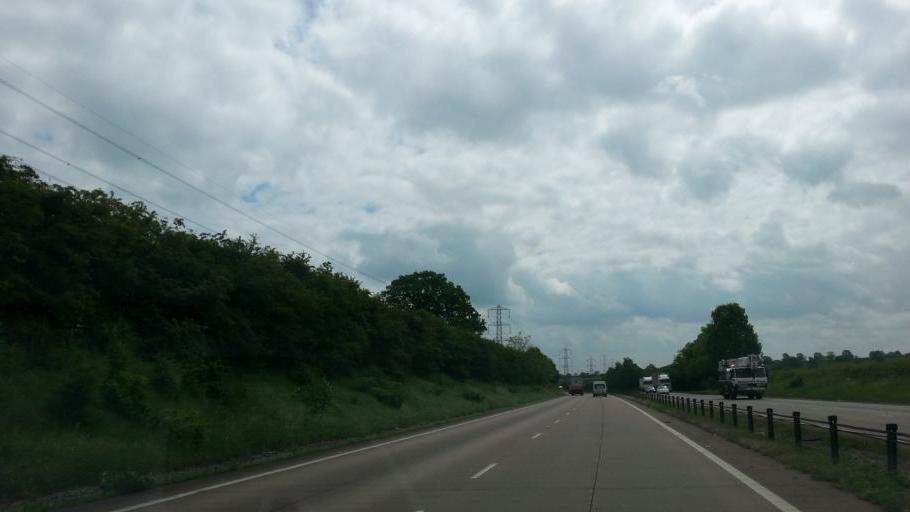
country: GB
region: England
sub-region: Staffordshire
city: Cheadle
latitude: 52.9254
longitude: -1.9412
